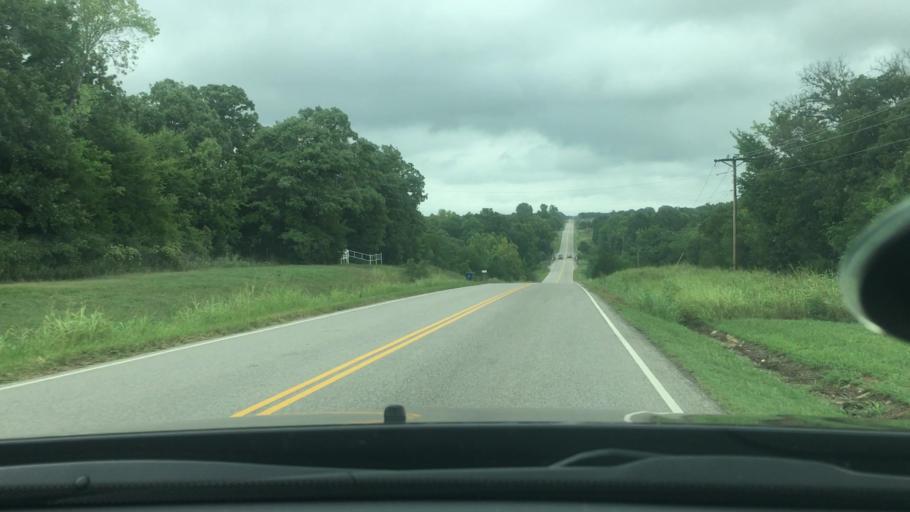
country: US
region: Oklahoma
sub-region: Bryan County
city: Calera
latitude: 33.9537
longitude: -96.5003
